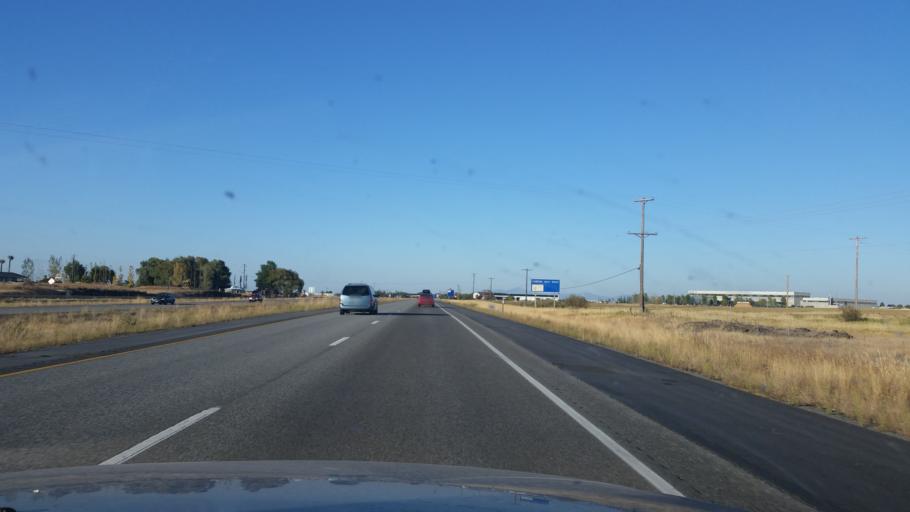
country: US
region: Washington
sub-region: Spokane County
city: Airway Heights
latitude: 47.5795
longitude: -117.5782
